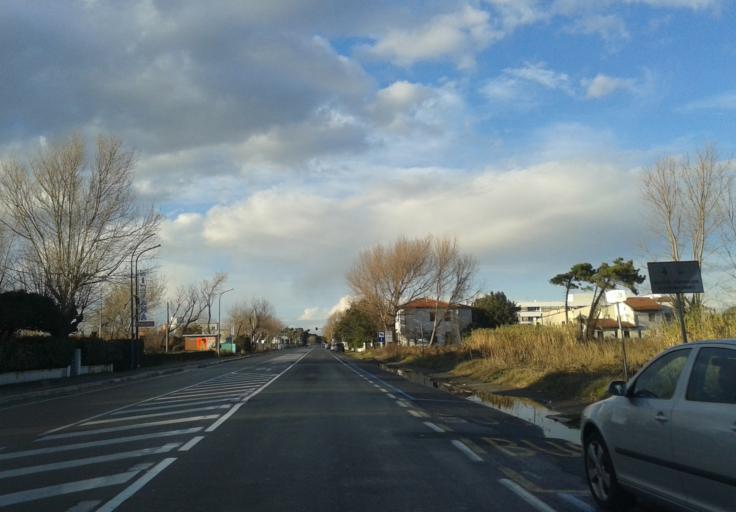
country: IT
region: Tuscany
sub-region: Province of Pisa
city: Marina di Pisa-Tirrenia-Calambrone
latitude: 43.5887
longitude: 10.2991
